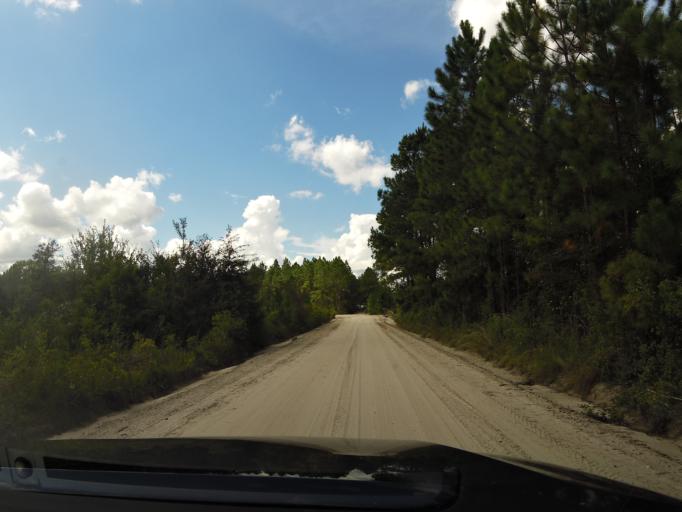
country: US
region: Georgia
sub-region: Brantley County
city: Nahunta
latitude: 31.0932
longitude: -82.0115
